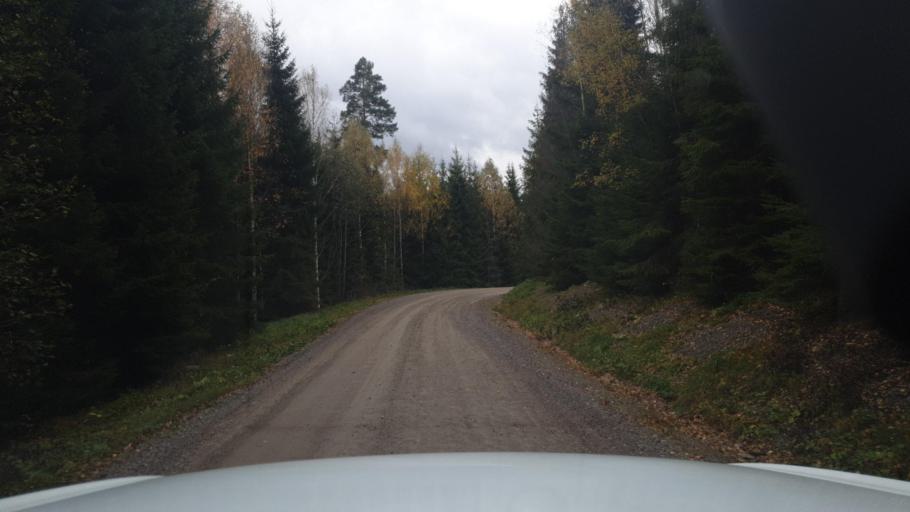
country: SE
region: Vaermland
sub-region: Arvika Kommun
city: Arvika
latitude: 59.9527
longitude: 12.6594
